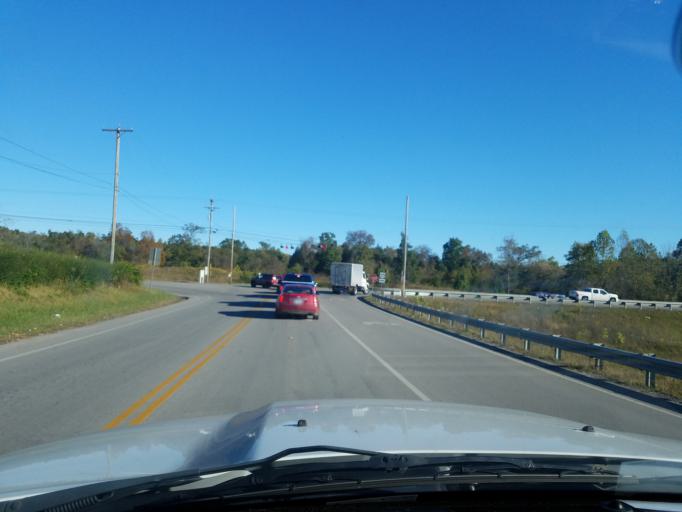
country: US
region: Kentucky
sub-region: Laurel County
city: North Corbin
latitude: 37.0314
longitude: -84.0631
